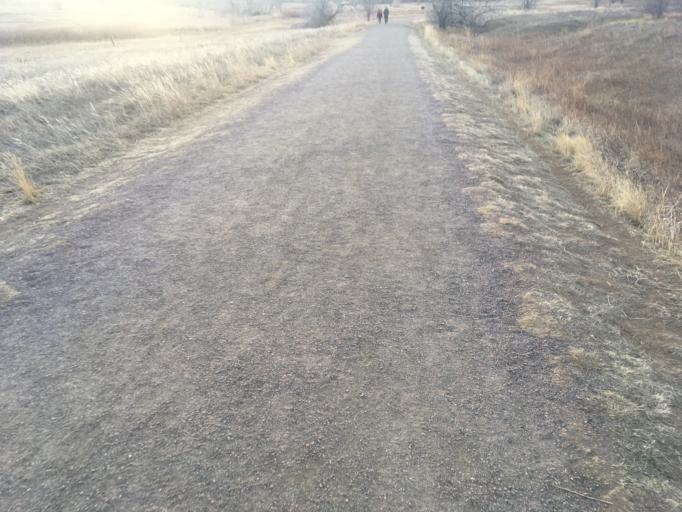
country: US
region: Colorado
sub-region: Boulder County
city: Lafayette
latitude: 40.0036
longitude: -105.0862
